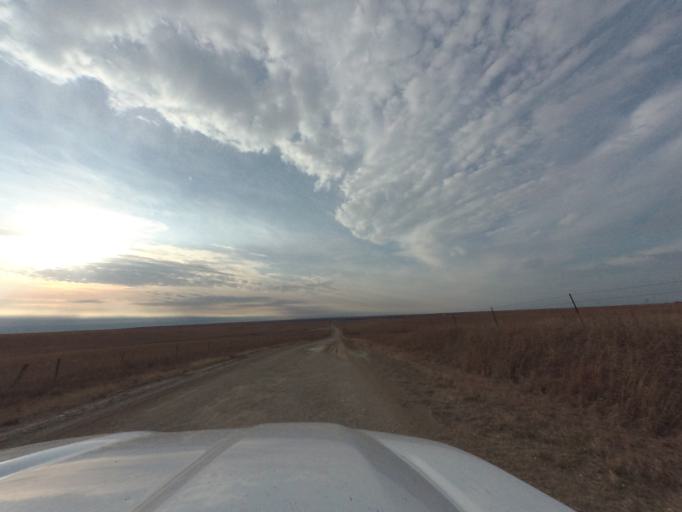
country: US
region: Kansas
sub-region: Morris County
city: Council Grove
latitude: 38.5113
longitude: -96.4100
